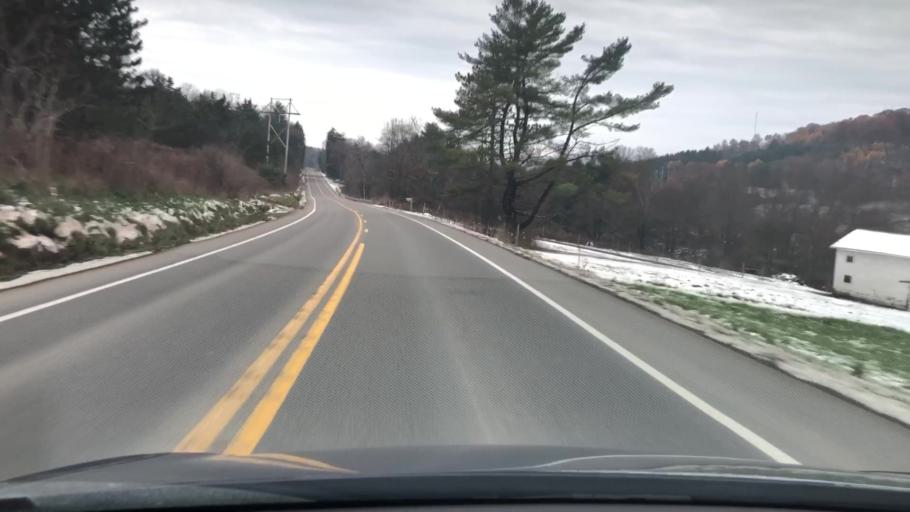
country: US
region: Pennsylvania
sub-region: Jefferson County
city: Brookville
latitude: 41.0526
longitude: -79.2519
